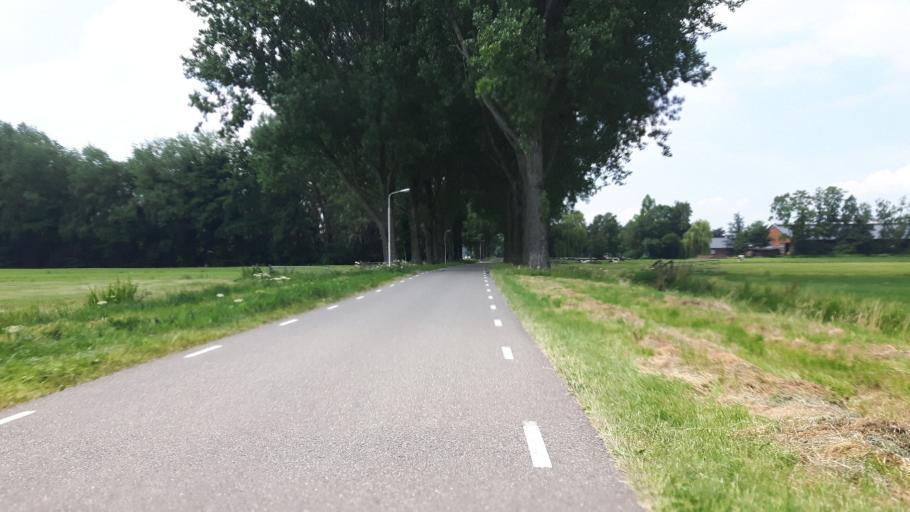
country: NL
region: Utrecht
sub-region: Gemeente Lopik
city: Lopik
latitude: 51.9189
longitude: 4.9691
